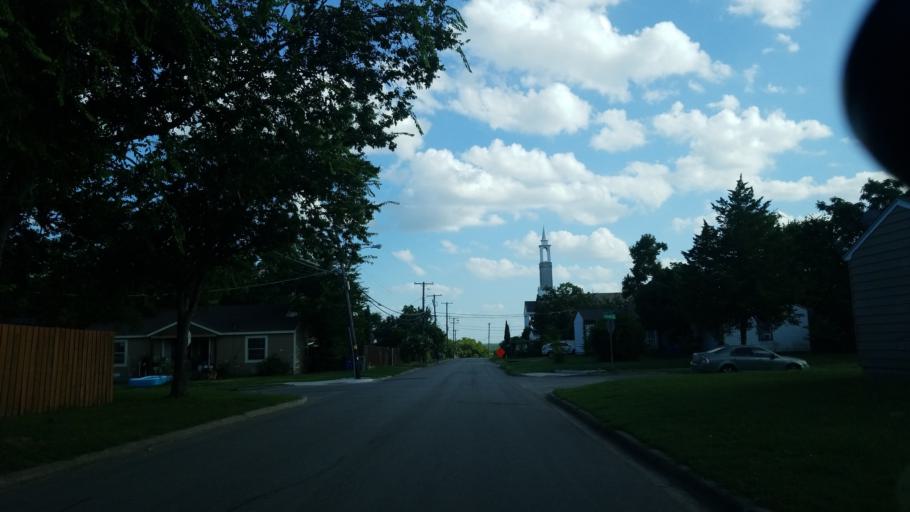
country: US
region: Texas
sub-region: Dallas County
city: Balch Springs
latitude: 32.7659
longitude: -96.7090
